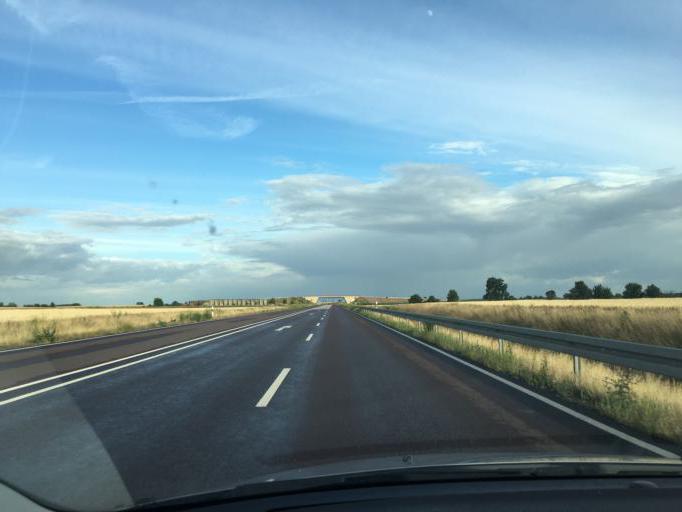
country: DE
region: Saxony-Anhalt
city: Wulfen
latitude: 51.7635
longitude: 11.9110
